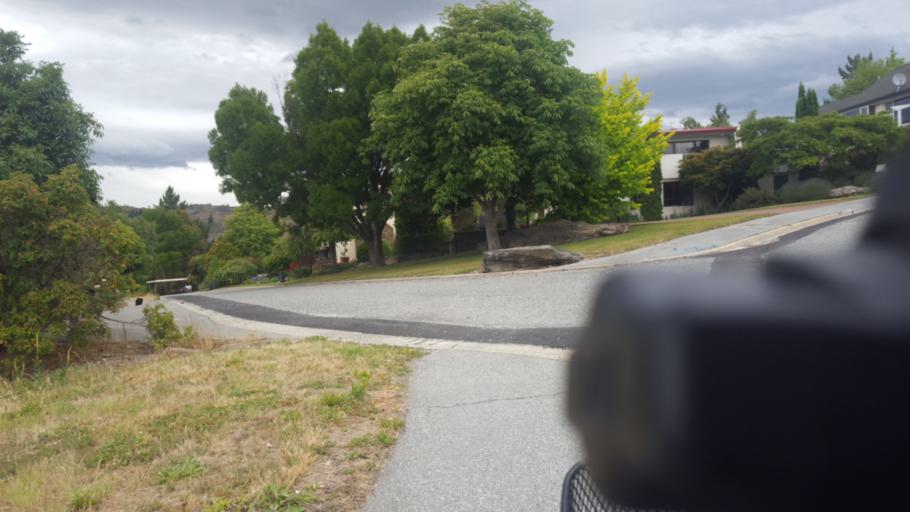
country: NZ
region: Otago
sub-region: Queenstown-Lakes District
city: Wanaka
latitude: -45.2629
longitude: 169.3811
